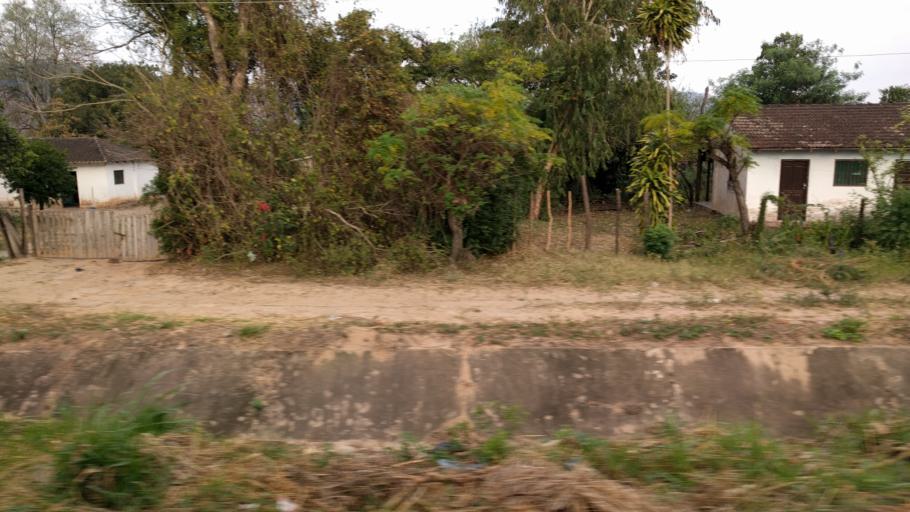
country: BO
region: Santa Cruz
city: Jorochito
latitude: -18.1161
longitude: -63.4607
